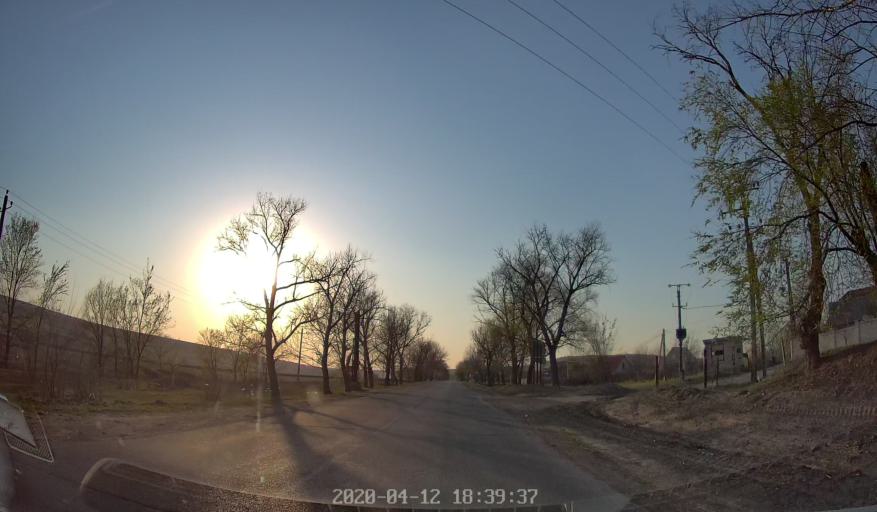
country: MD
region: Chisinau
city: Ciorescu
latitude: 47.1288
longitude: 28.9820
